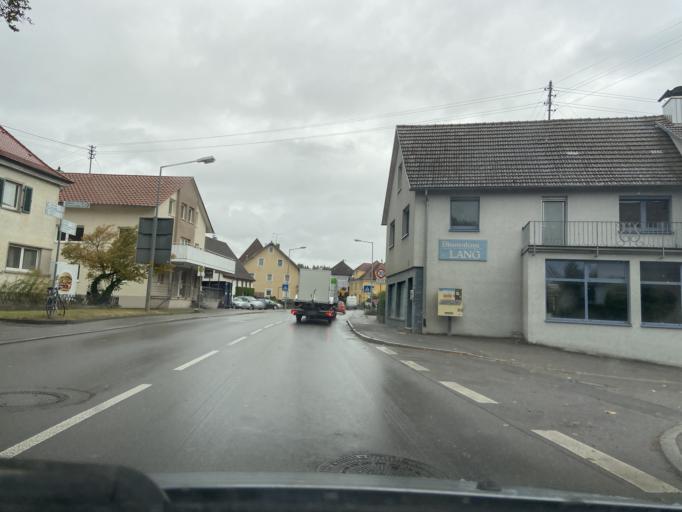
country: DE
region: Baden-Wuerttemberg
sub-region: Tuebingen Region
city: Krauchenwies
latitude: 48.0186
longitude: 9.2472
